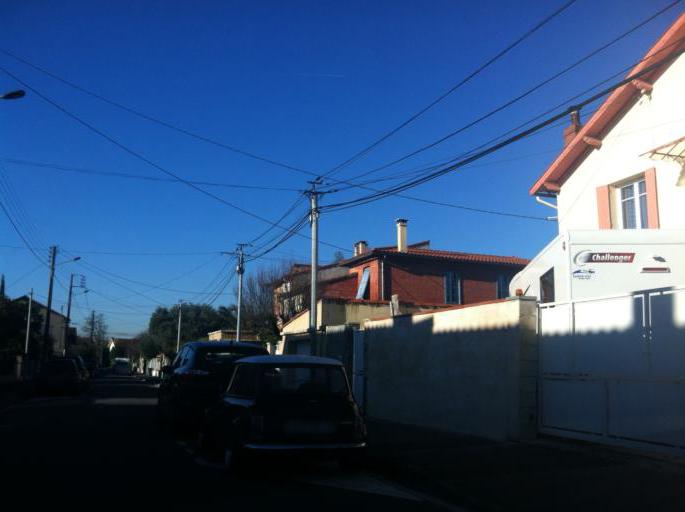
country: FR
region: Midi-Pyrenees
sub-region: Departement de la Haute-Garonne
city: Toulouse
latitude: 43.5813
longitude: 1.4688
